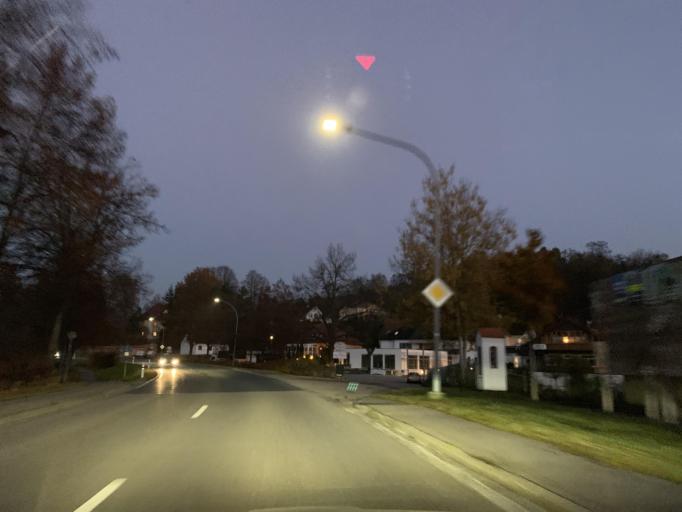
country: DE
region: Bavaria
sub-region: Upper Palatinate
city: Bodenwohr
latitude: 49.2705
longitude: 12.3068
